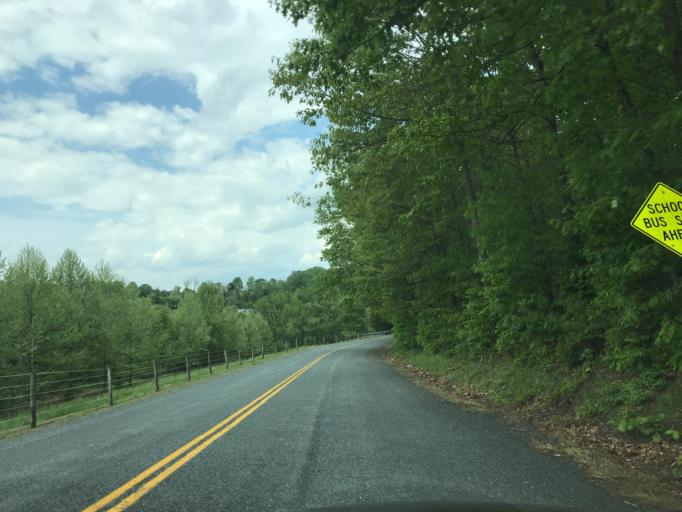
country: US
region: Maryland
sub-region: Harford County
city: Bel Air North
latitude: 39.6169
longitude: -76.3490
